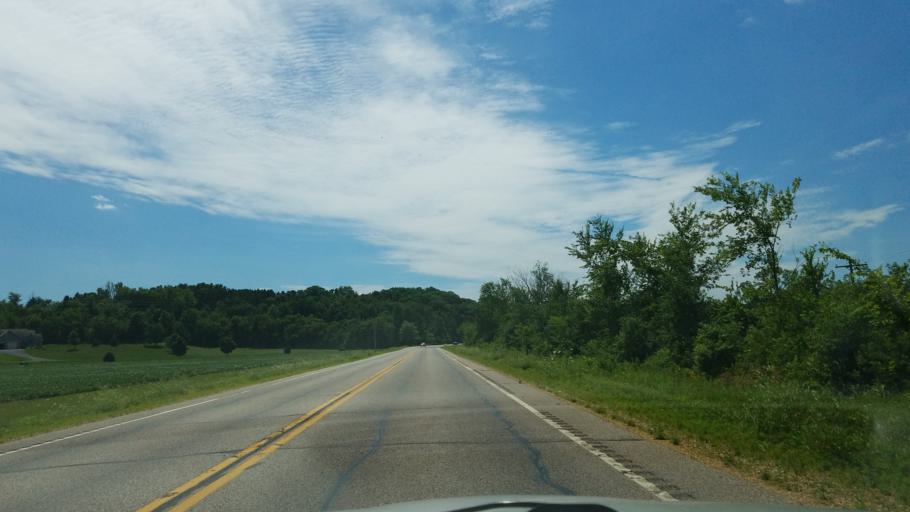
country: US
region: Wisconsin
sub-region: Saint Croix County
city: Glenwood City
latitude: 45.0354
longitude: -92.1830
